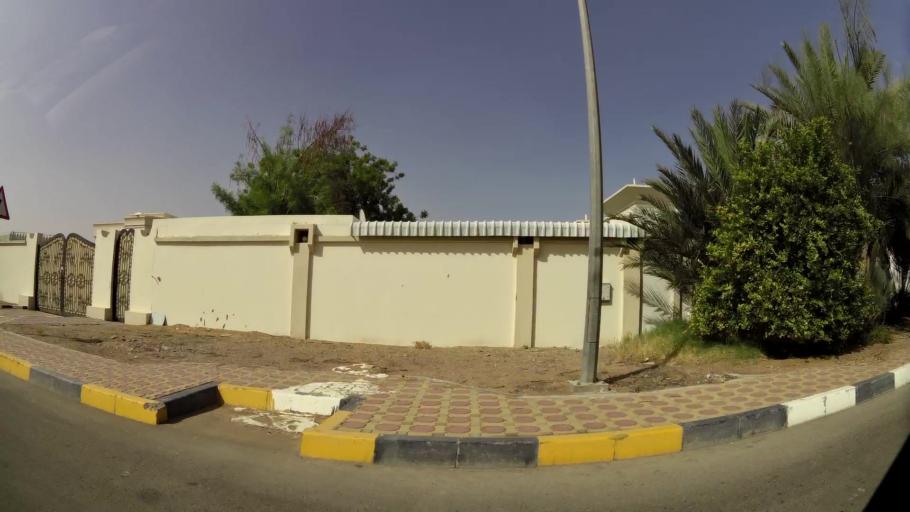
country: AE
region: Abu Dhabi
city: Al Ain
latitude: 24.2505
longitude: 55.6898
